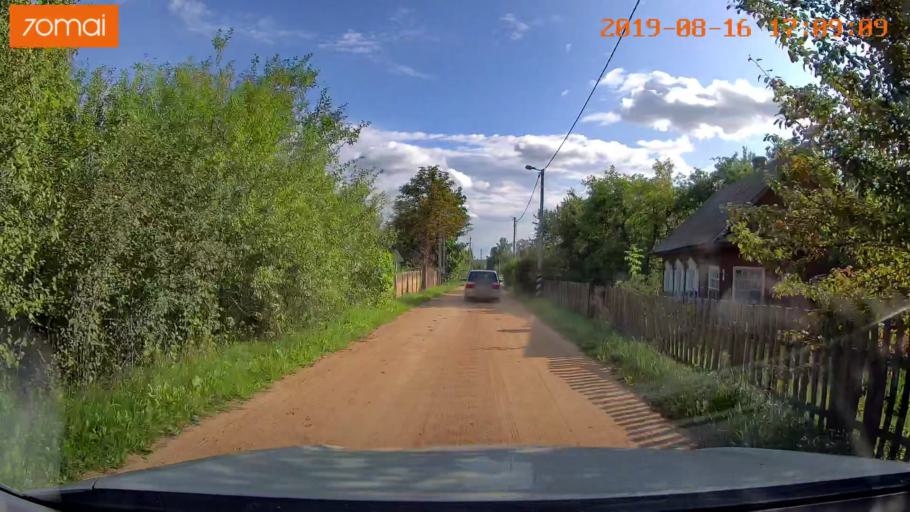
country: BY
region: Mogilev
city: Hlusha
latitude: 53.2157
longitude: 28.9255
